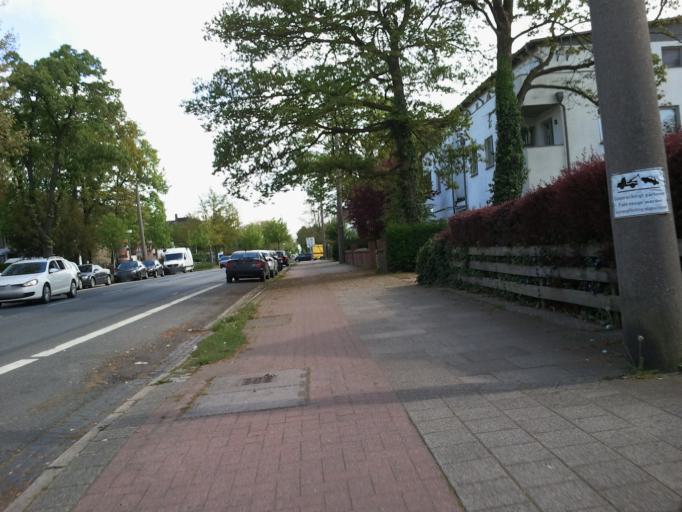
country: DE
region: Lower Saxony
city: Ritterhude
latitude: 53.1282
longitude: 8.7449
